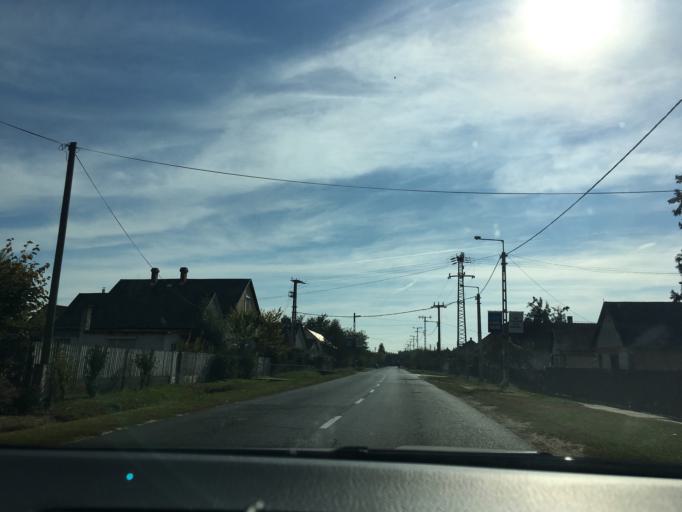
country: HU
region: Hajdu-Bihar
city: Nyirabrany
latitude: 47.5980
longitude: 22.0550
